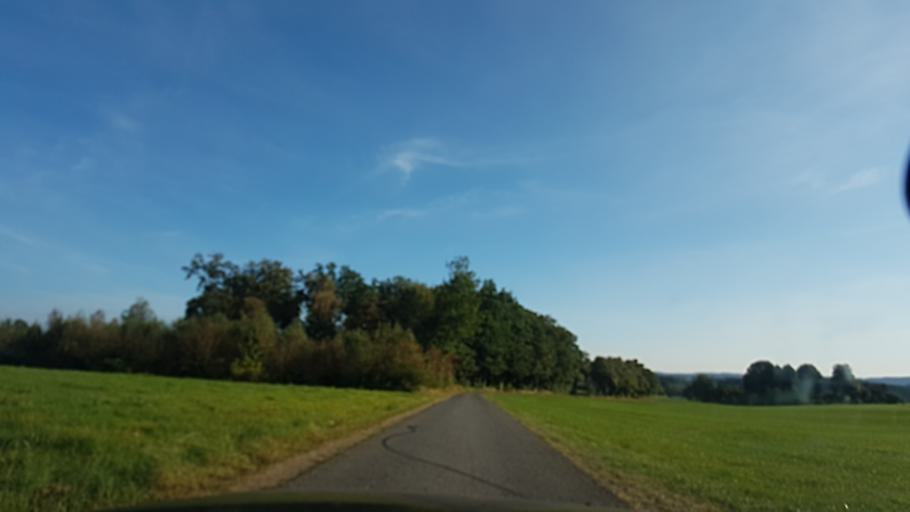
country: DE
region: North Rhine-Westphalia
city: Halver
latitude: 51.1526
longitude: 7.5012
